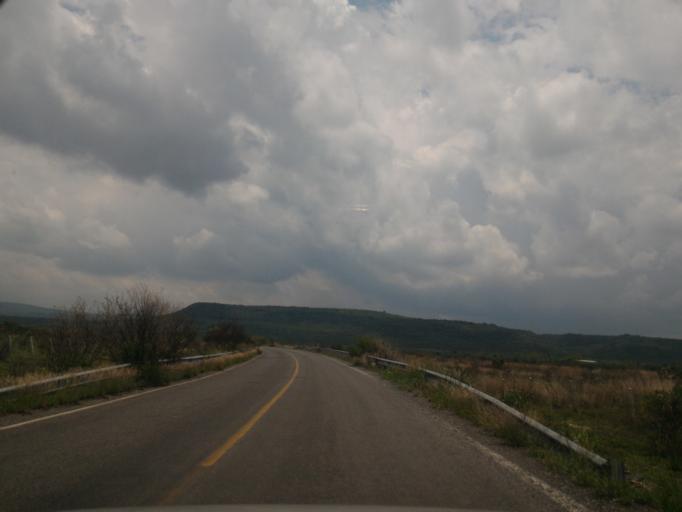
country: MX
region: Jalisco
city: San Diego de Alejandria
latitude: 20.8925
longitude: -101.9688
